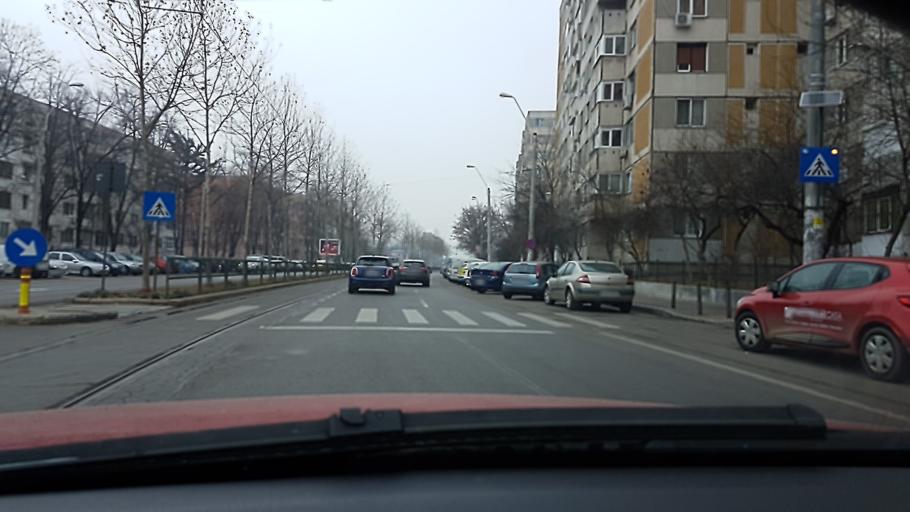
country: RO
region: Ilfov
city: Dobroesti
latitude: 44.4214
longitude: 26.1753
